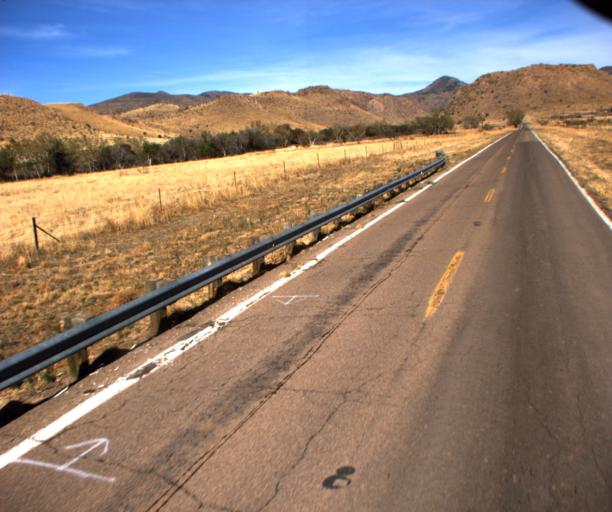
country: US
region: Arizona
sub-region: Cochise County
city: Willcox
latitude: 32.0067
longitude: -109.4033
